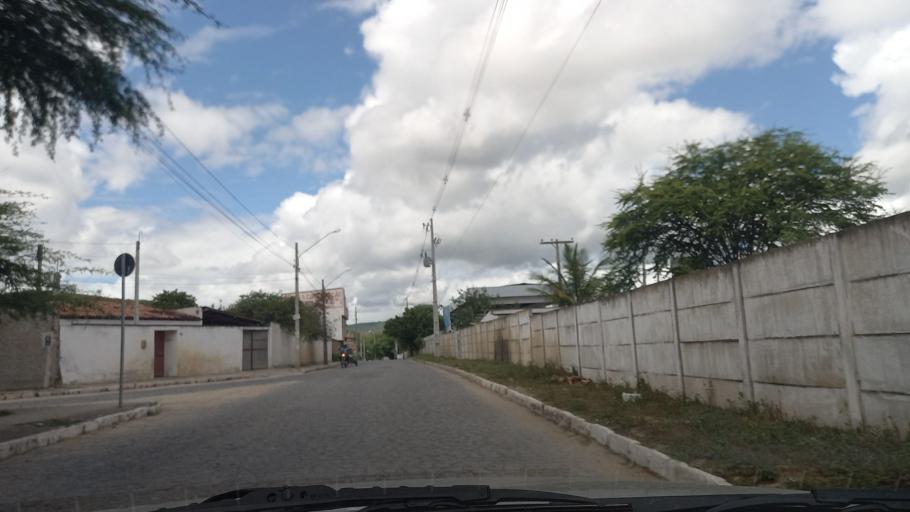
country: BR
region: Pernambuco
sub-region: Caruaru
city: Caruaru
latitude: -8.2816
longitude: -35.9378
